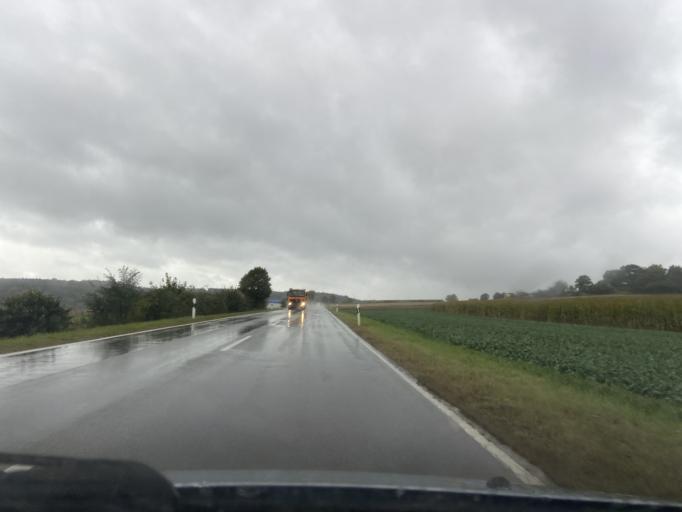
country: DE
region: Baden-Wuerttemberg
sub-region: Tuebingen Region
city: Scheer
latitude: 48.0717
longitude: 9.2841
